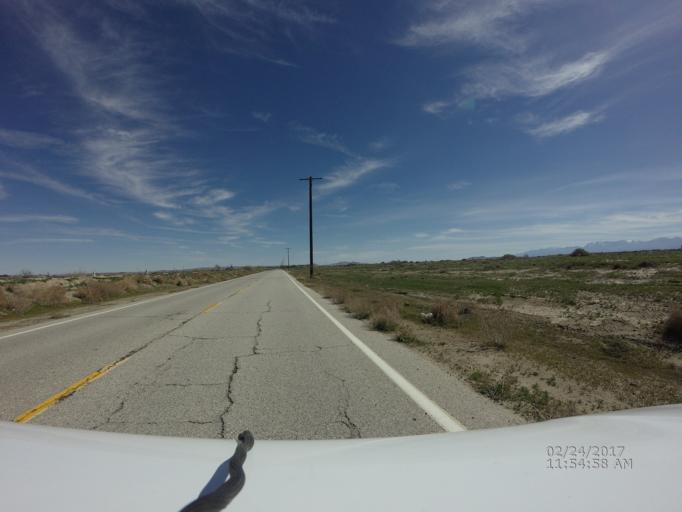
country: US
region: California
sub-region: Los Angeles County
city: Lancaster
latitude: 34.7192
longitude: -118.0292
